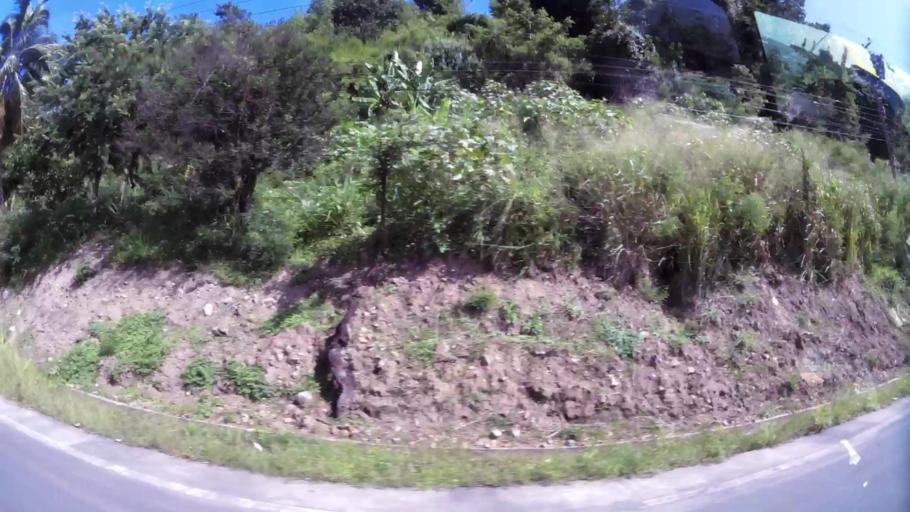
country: DM
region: Saint George
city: Roseau
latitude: 15.3171
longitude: -61.3900
